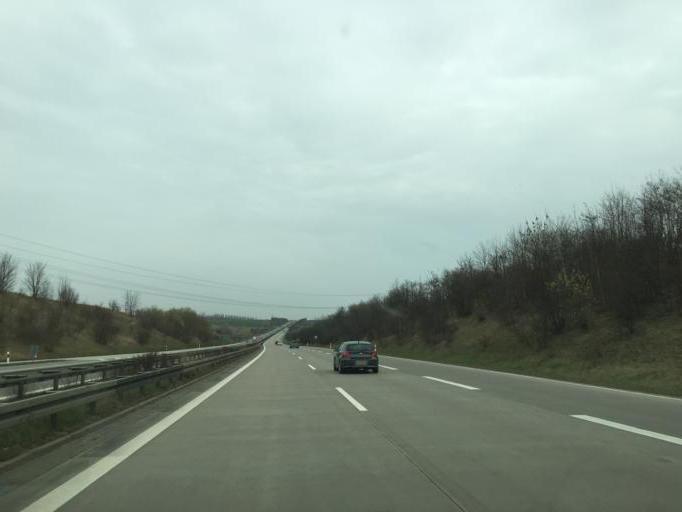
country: DE
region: Mecklenburg-Vorpommern
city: Roggentin
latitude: 54.0523
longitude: 12.1986
